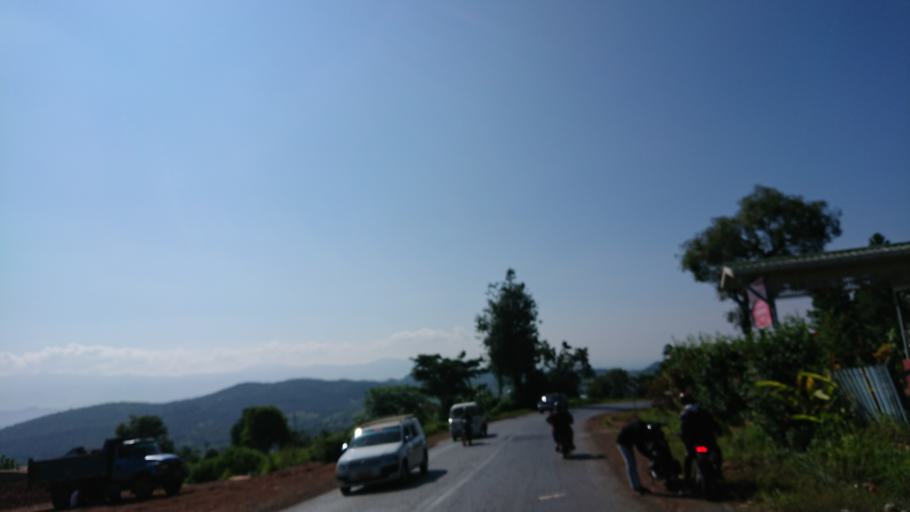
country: MM
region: Shan
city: Taunggyi
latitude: 20.7465
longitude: 97.0911
